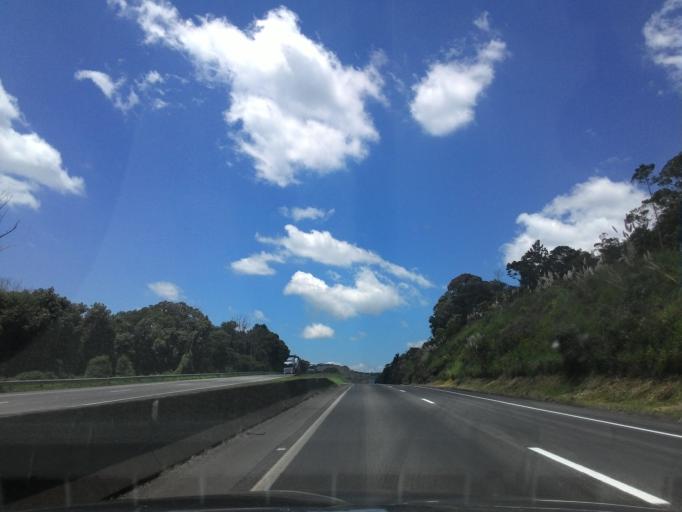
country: BR
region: Sao Paulo
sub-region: Cajati
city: Cajati
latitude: -24.9705
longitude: -48.3796
